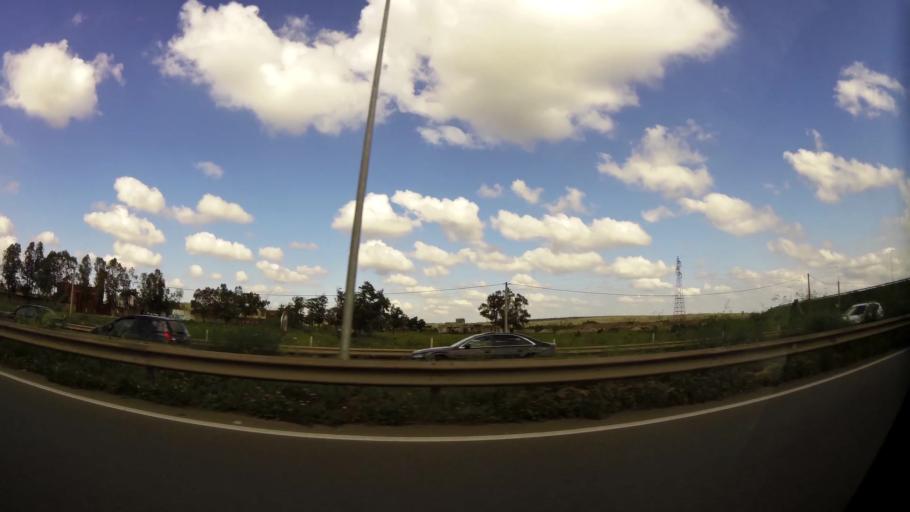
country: MA
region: Grand Casablanca
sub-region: Nouaceur
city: Bouskoura
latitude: 33.4390
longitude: -7.6299
